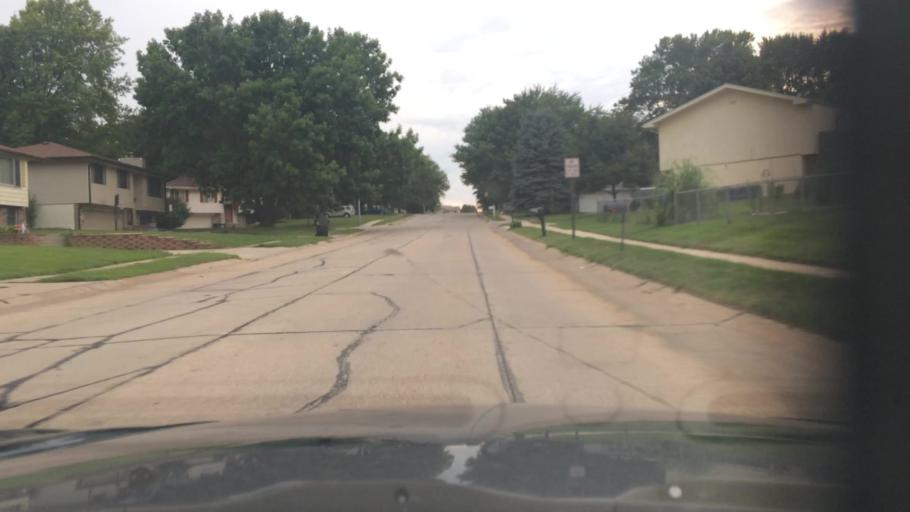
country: US
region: Nebraska
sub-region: Sarpy County
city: La Vista
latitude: 41.1840
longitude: -96.0544
